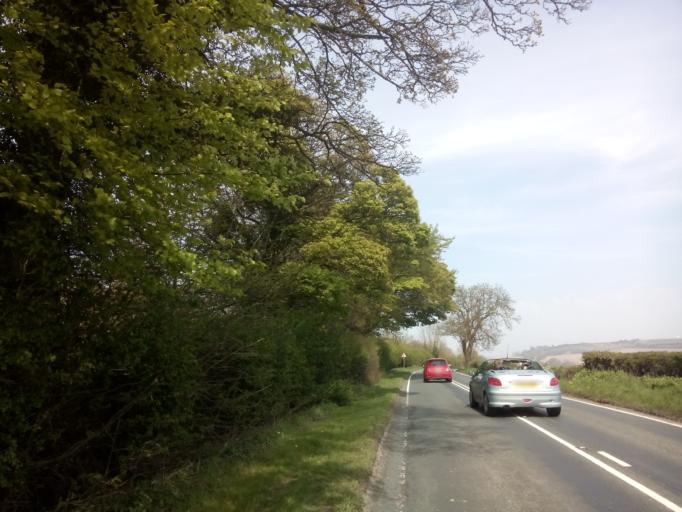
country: GB
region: England
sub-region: County Durham
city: West Rainton
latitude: 54.7963
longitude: -1.5045
